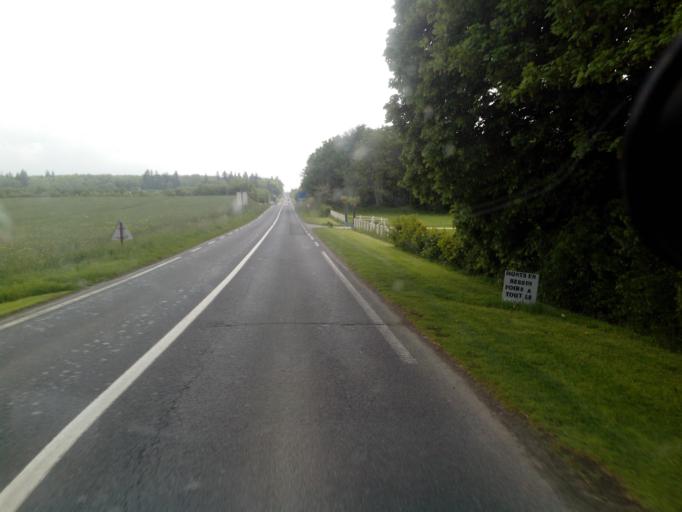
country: FR
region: Lower Normandy
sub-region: Departement du Calvados
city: Villers-Bocage
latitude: 49.0718
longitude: -0.6591
